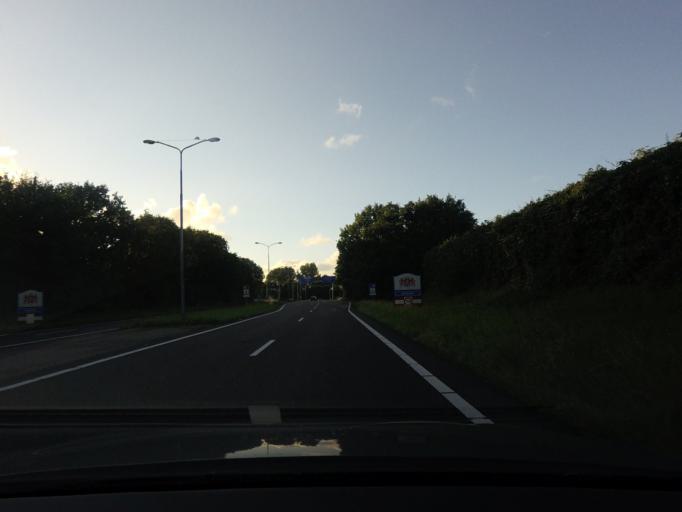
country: NL
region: North Holland
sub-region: Gemeente Alkmaar
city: Alkmaar
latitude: 52.6482
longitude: 4.7662
